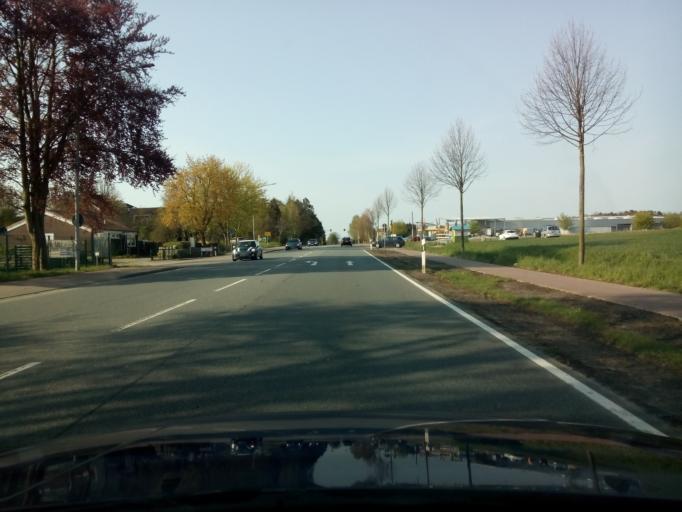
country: DE
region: Lower Saxony
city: Syke
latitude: 52.9290
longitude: 8.8242
